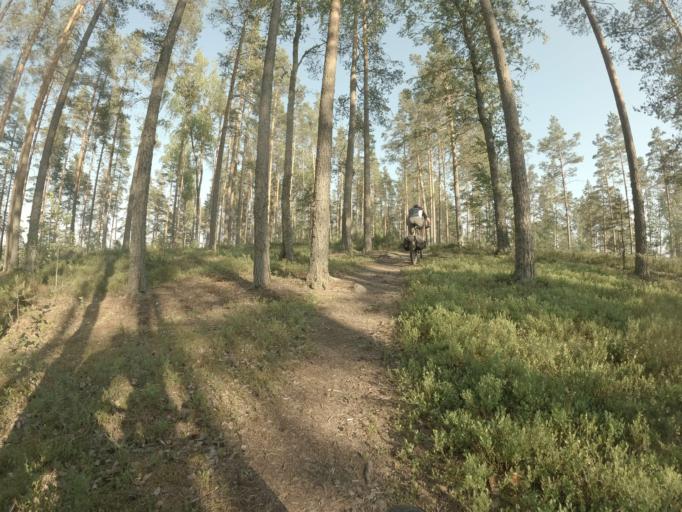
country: RU
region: Leningrad
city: Veshchevo
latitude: 60.4404
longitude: 29.2305
